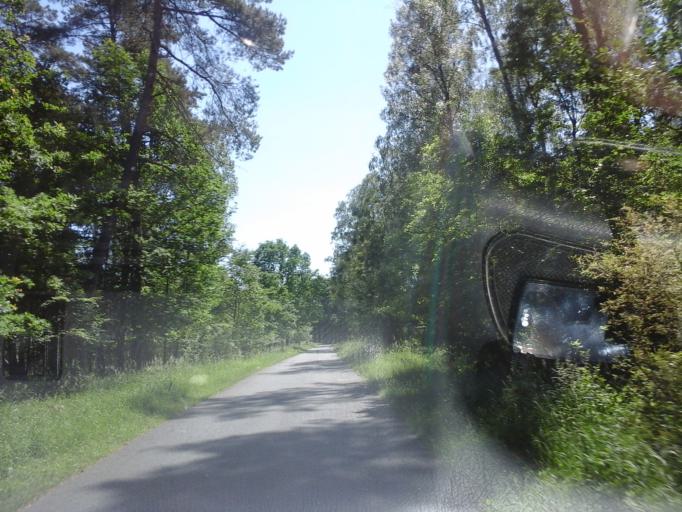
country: PL
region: West Pomeranian Voivodeship
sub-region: Powiat drawski
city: Kalisz Pomorski
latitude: 53.1138
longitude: 15.9221
